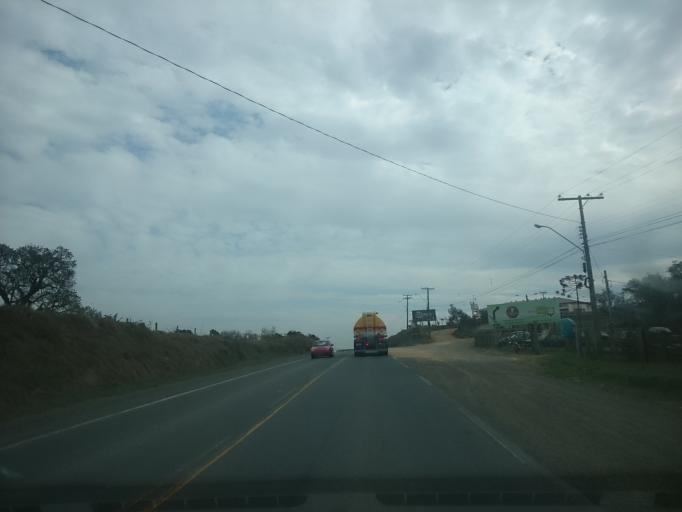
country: BR
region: Santa Catarina
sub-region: Lages
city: Lages
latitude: -27.7716
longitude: -50.3213
